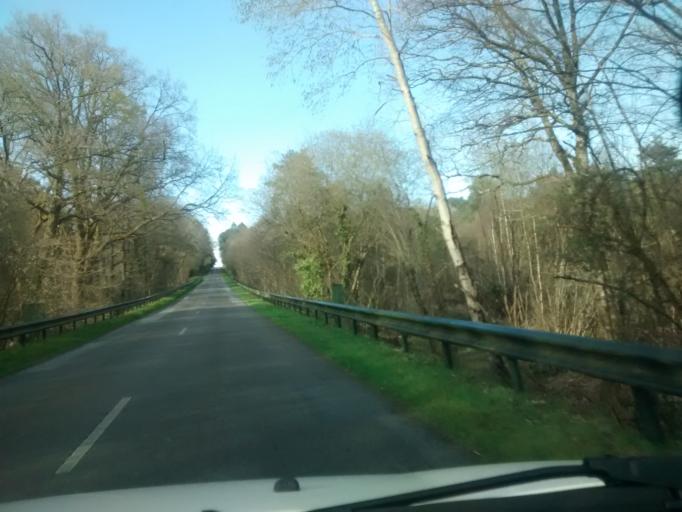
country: FR
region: Brittany
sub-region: Departement d'Ille-et-Vilaine
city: La Bouexiere
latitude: 48.1565
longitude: -1.4424
